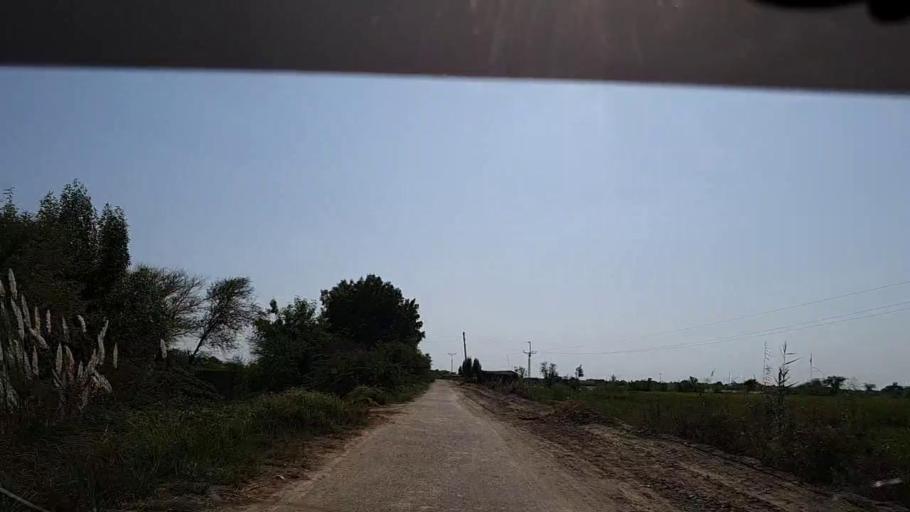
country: PK
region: Sindh
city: Badin
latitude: 24.6332
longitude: 68.7853
